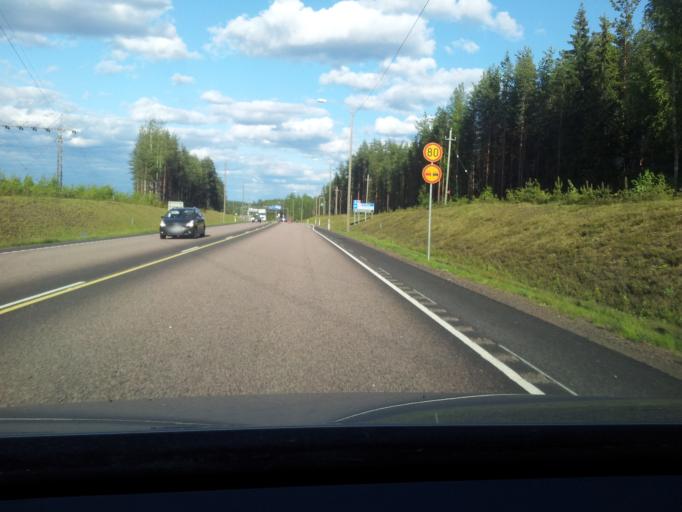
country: FI
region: Kymenlaakso
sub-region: Kotka-Hamina
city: Hamina
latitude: 60.9036
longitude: 27.1211
